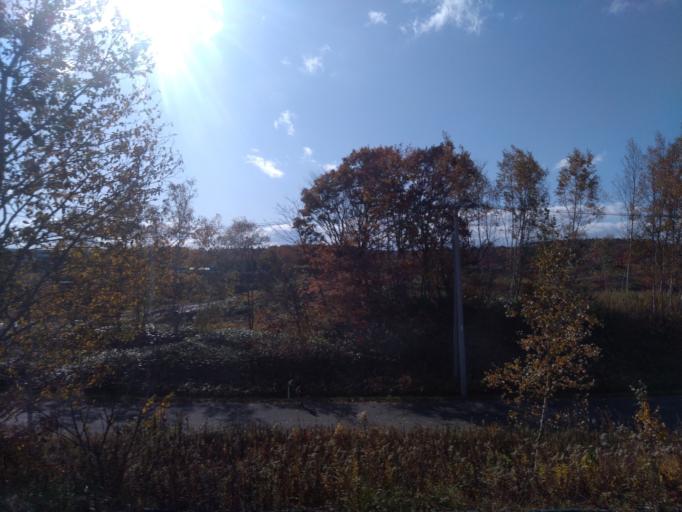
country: JP
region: Hokkaido
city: Kitahiroshima
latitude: 42.9912
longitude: 141.5555
